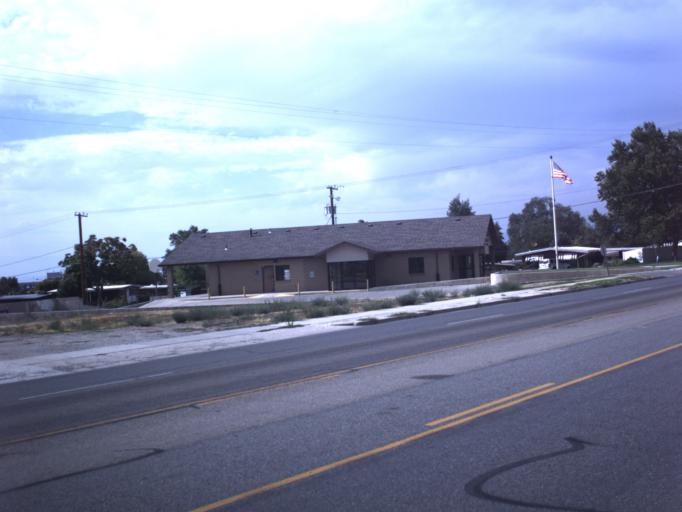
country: US
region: Utah
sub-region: Davis County
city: North Salt Lake
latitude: 40.8475
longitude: -111.9071
